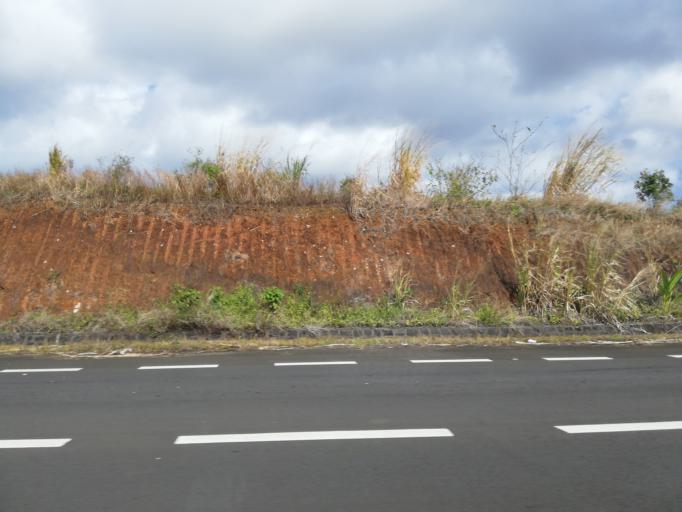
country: MU
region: Grand Port
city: Mahebourg
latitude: -20.4027
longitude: 57.6783
